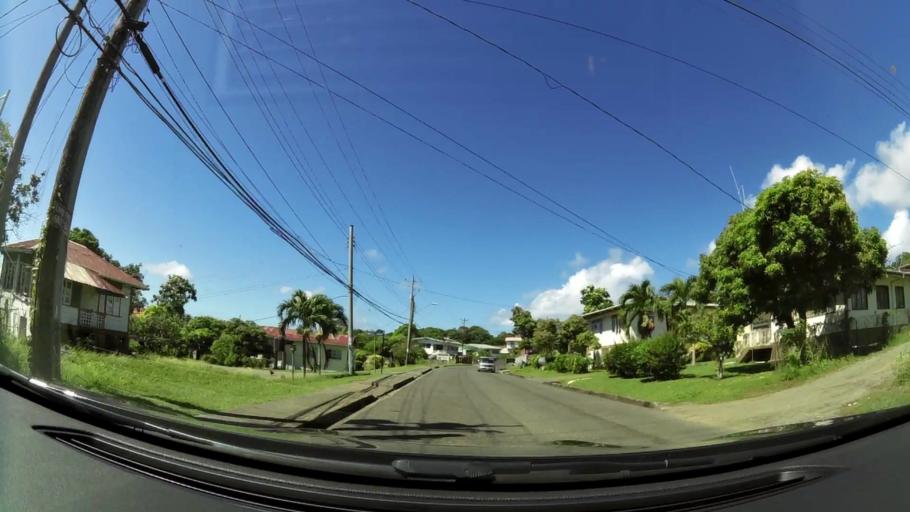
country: TT
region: Tobago
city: Scarborough
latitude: 11.1691
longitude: -60.7804
